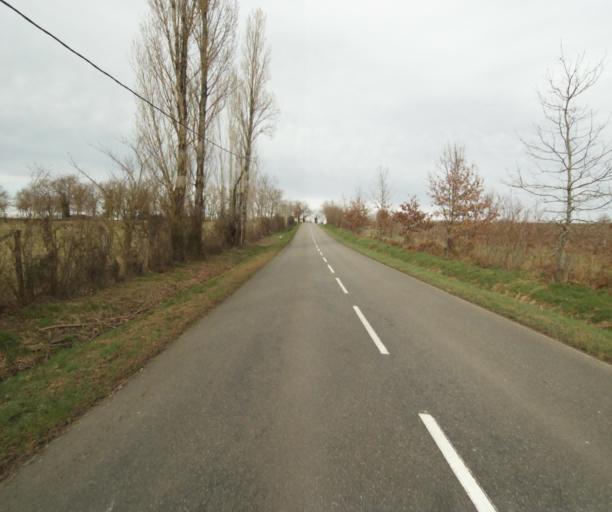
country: FR
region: Aquitaine
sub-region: Departement des Landes
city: Gabarret
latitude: 43.9620
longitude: 0.0052
